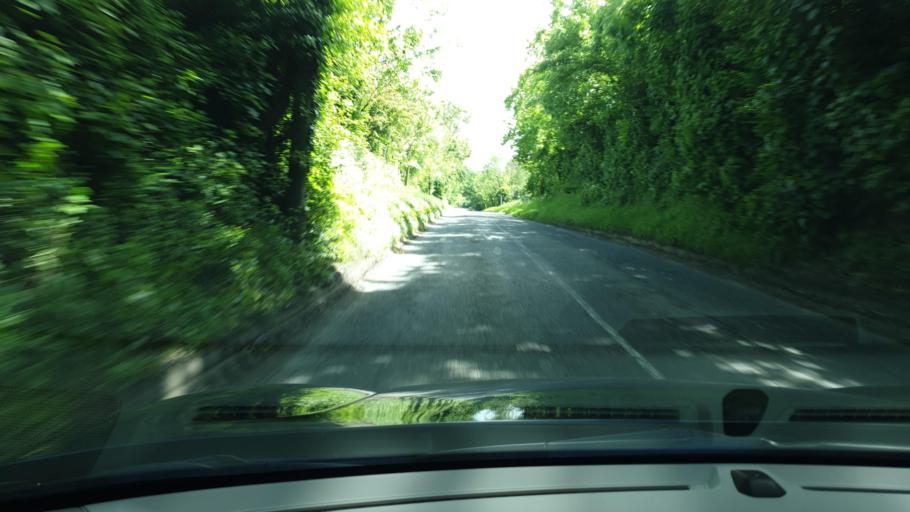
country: IE
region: Ulster
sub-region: An Cabhan
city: Kingscourt
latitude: 53.8336
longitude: -6.7635
